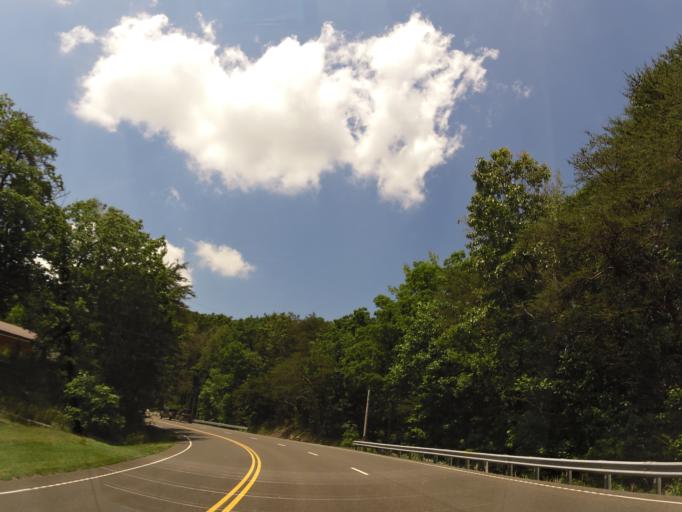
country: US
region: Tennessee
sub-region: Rhea County
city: Dayton
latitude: 35.5237
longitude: -85.0397
